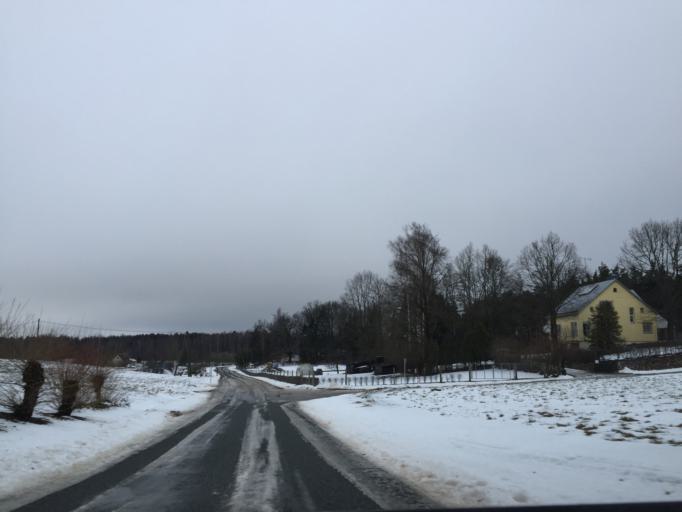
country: LV
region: Krimulda
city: Ragana
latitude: 57.1833
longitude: 24.6973
